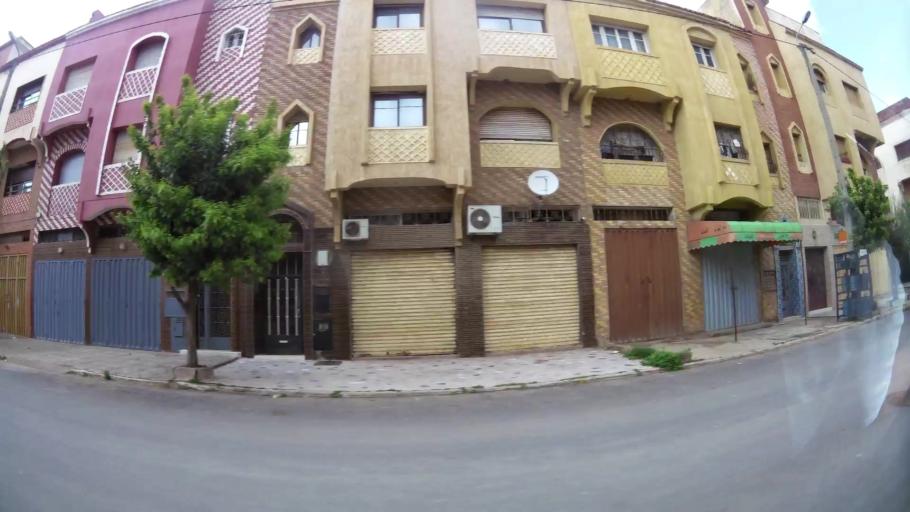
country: MA
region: Grand Casablanca
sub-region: Mediouna
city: Mediouna
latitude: 33.3762
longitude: -7.5337
